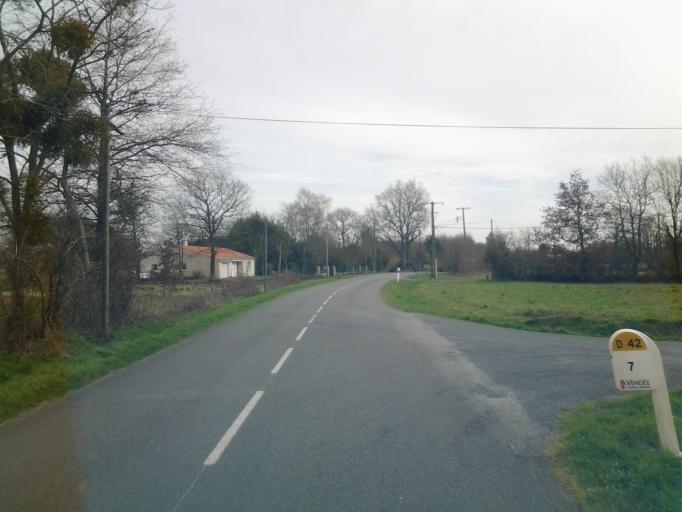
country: FR
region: Pays de la Loire
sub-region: Departement de la Vendee
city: Venansault
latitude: 46.6860
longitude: -1.5291
